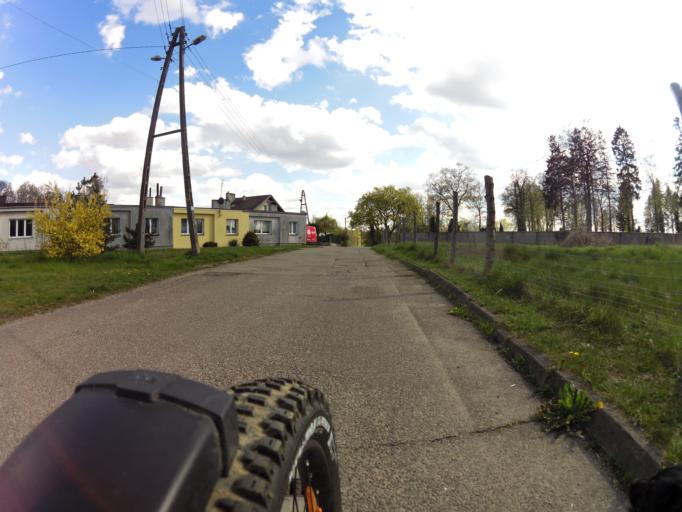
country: PL
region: West Pomeranian Voivodeship
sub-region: Powiat gryficki
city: Ploty
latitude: 53.7994
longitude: 15.2630
